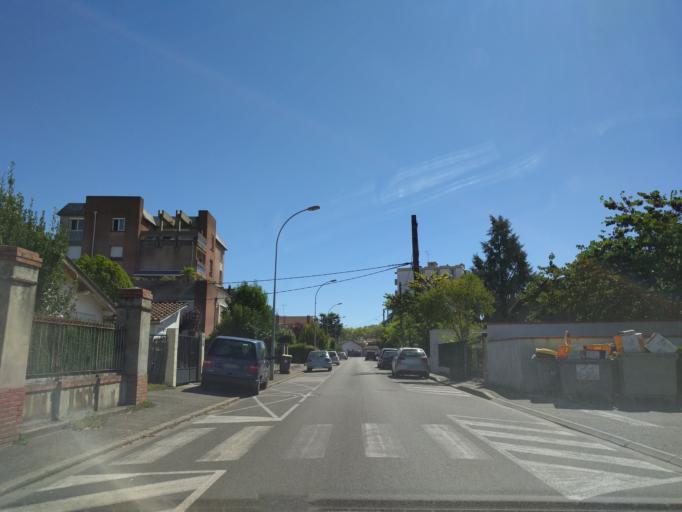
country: FR
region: Midi-Pyrenees
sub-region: Departement du Tarn-et-Garonne
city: Montauban
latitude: 44.0174
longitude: 1.3663
